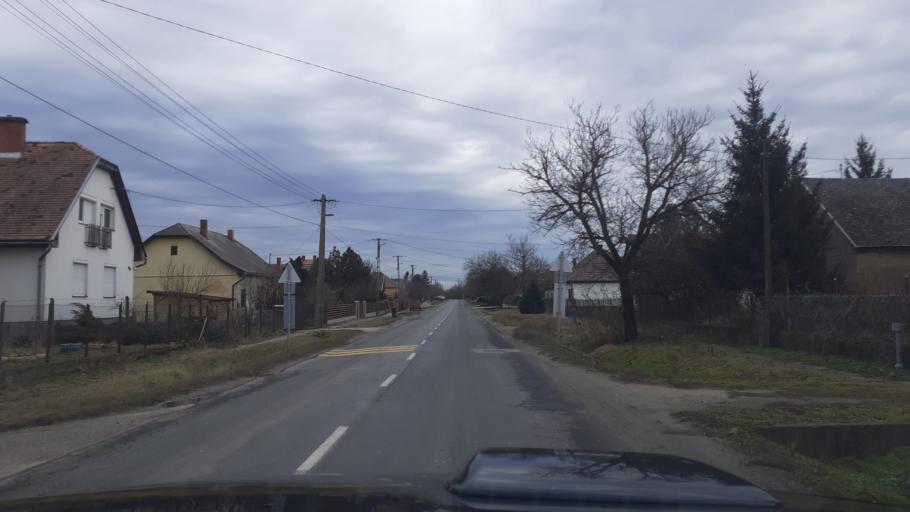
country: HU
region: Fejer
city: Sarosd
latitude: 47.0360
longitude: 18.6577
